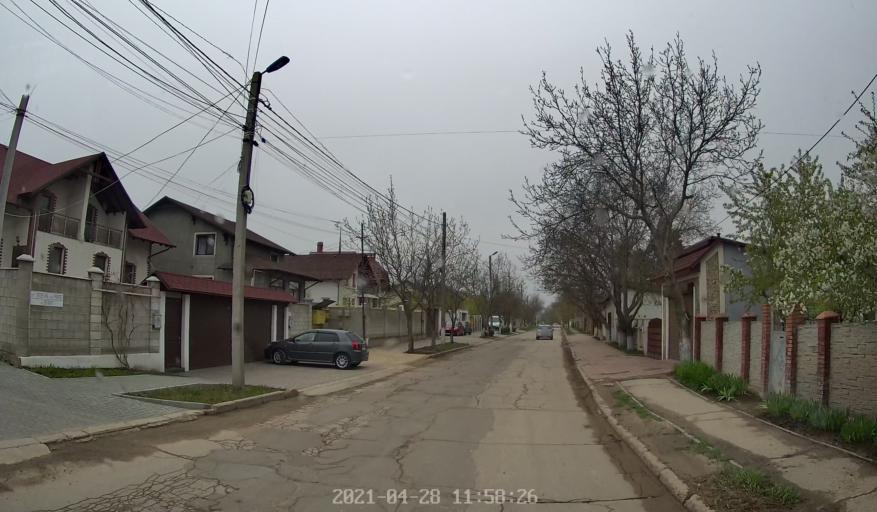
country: MD
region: Chisinau
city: Singera
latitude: 46.9791
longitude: 28.9338
